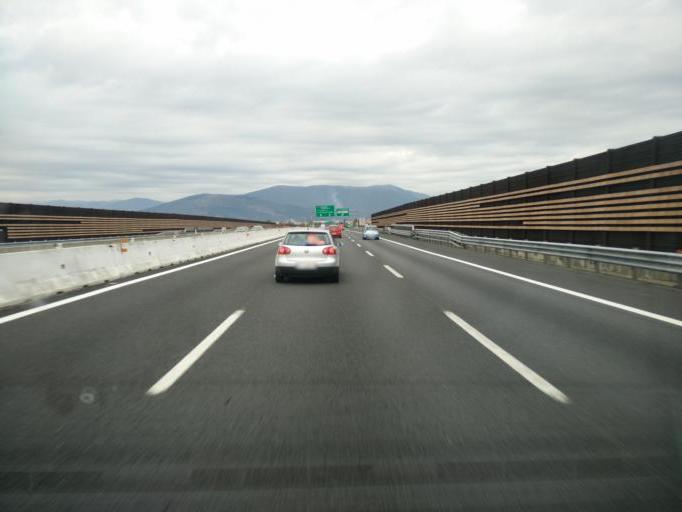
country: IT
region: Tuscany
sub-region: Province of Florence
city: Campi Bisenzio
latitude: 43.8165
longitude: 11.1515
